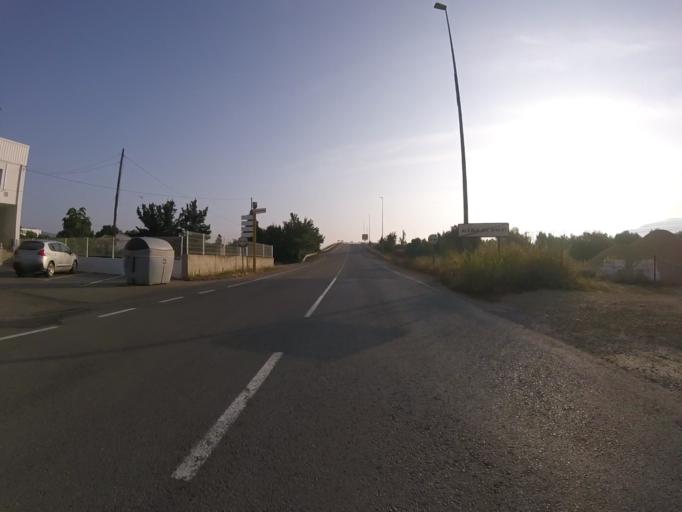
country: ES
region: Valencia
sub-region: Provincia de Castello
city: Alcala de Xivert
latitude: 40.3110
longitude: 0.2304
